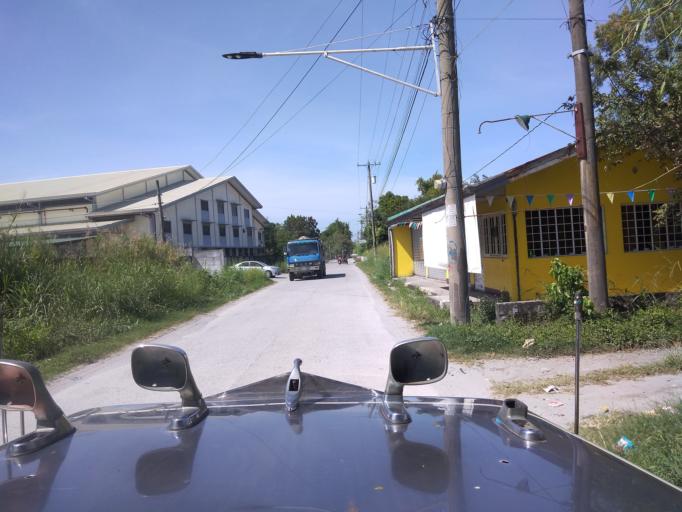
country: PH
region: Central Luzon
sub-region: Province of Pampanga
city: Bacolor
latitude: 15.0155
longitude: 120.6605
